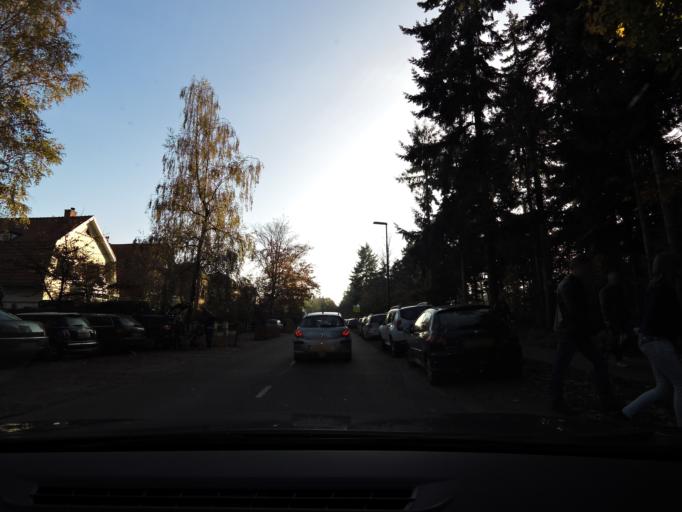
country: NL
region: North Brabant
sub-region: Gemeente Breda
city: Breda
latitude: 51.5531
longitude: 4.7799
